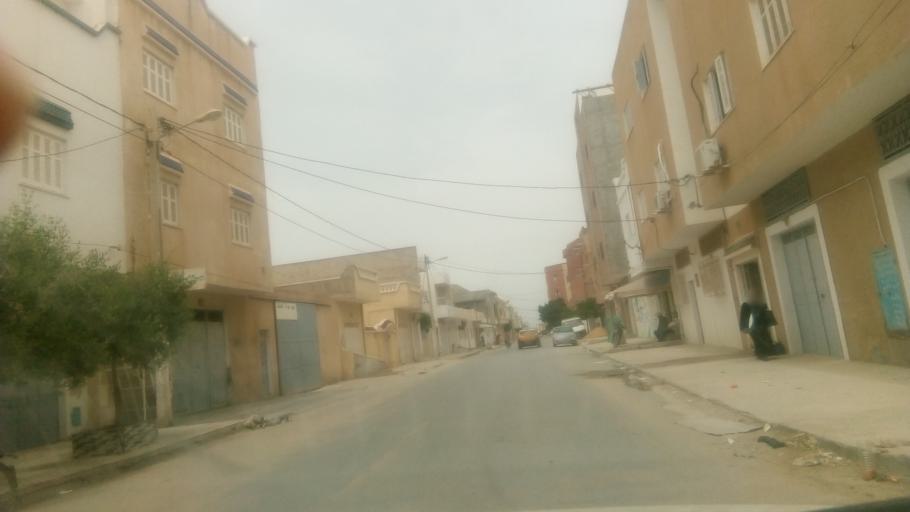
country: TN
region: Al Qayrawan
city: Kairouan
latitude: 35.6660
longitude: 10.0841
